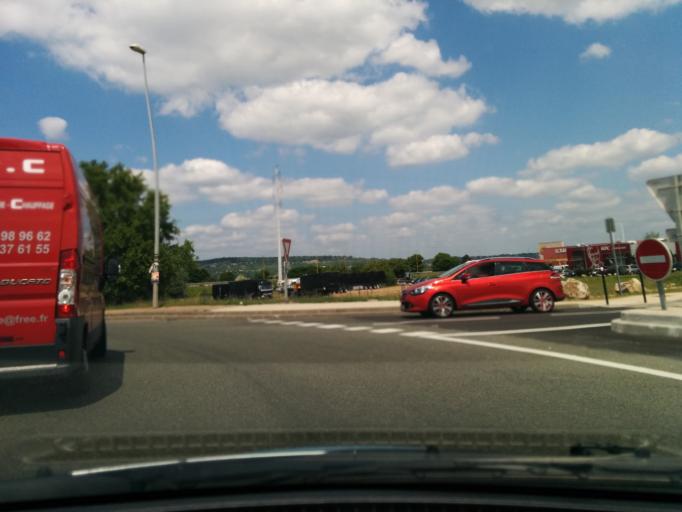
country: FR
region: Ile-de-France
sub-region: Departement des Yvelines
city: Flins-sur-Seine
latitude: 48.9668
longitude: 1.8656
